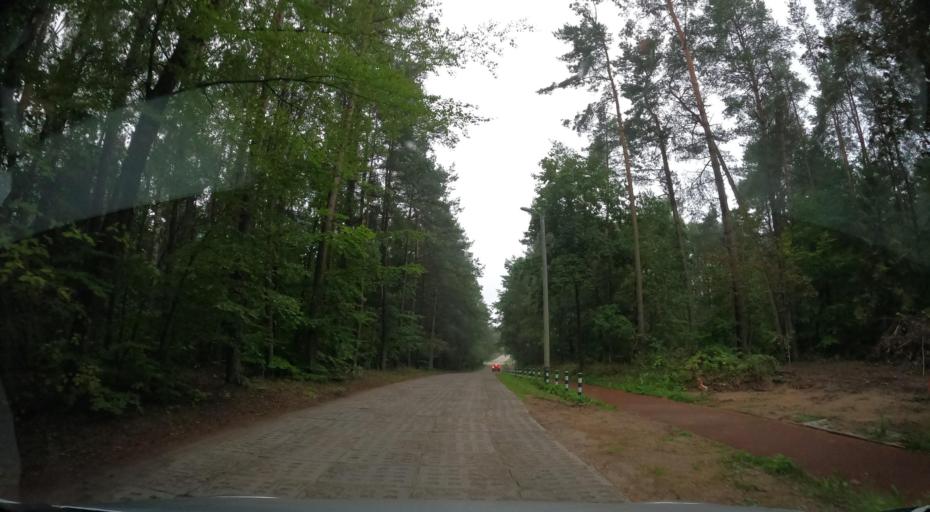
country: PL
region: Pomeranian Voivodeship
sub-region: Powiat kartuski
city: Chwaszczyno
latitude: 54.4339
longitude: 18.4181
